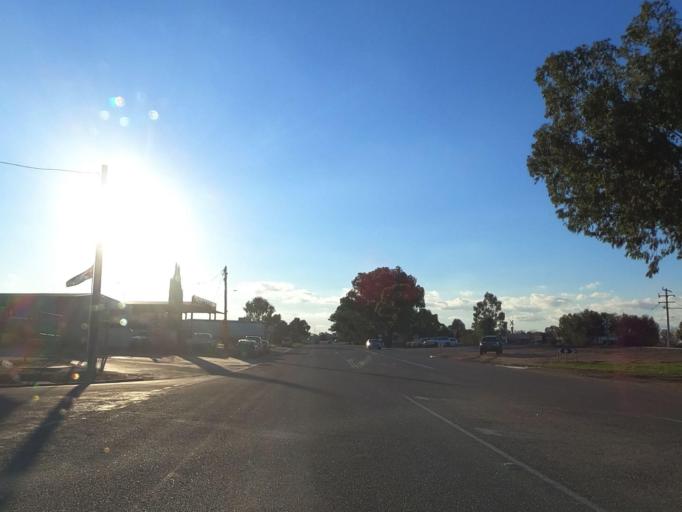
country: AU
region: Victoria
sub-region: Swan Hill
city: Swan Hill
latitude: -35.3307
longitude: 143.5566
